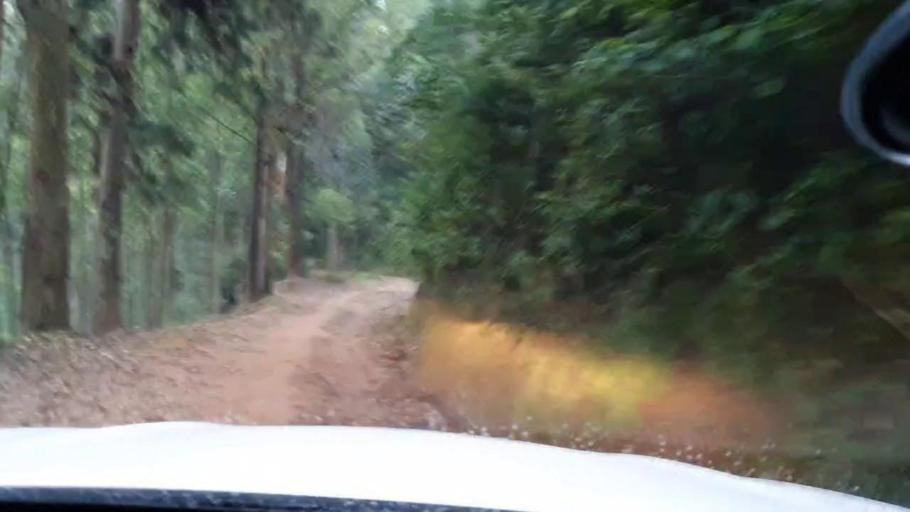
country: RW
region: Western Province
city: Cyangugu
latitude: -2.4107
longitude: 29.1951
